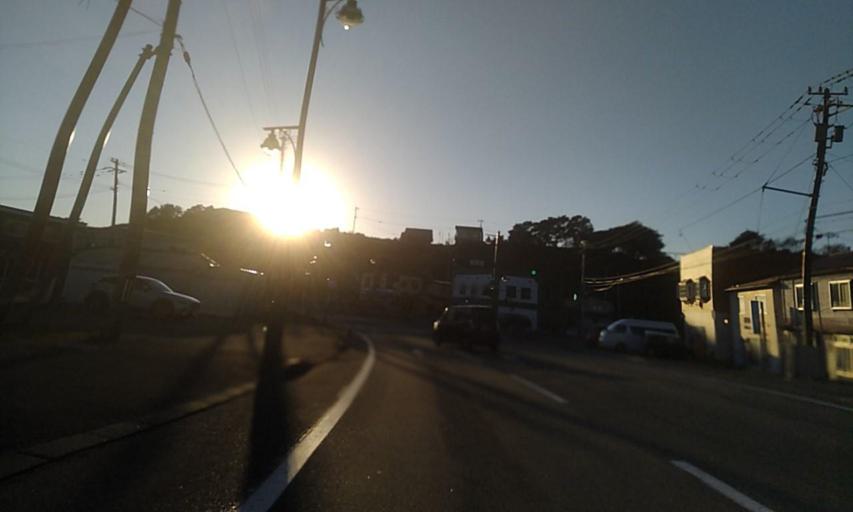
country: JP
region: Hokkaido
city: Shizunai-furukawacho
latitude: 42.1280
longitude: 142.9285
